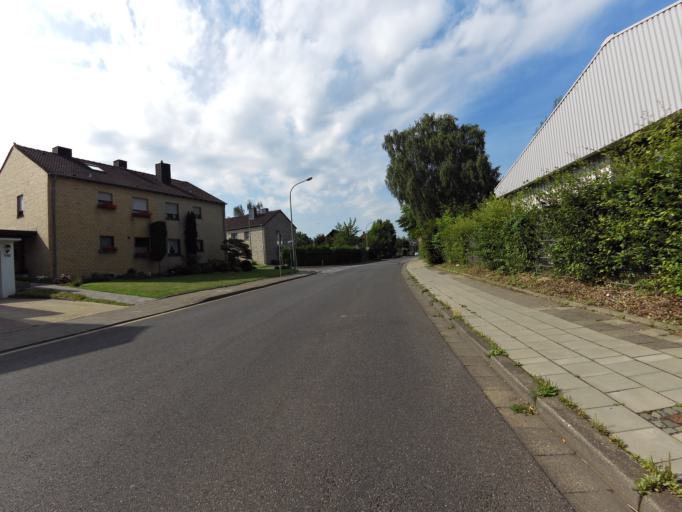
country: DE
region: North Rhine-Westphalia
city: Baesweiler
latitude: 50.9216
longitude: 6.2104
